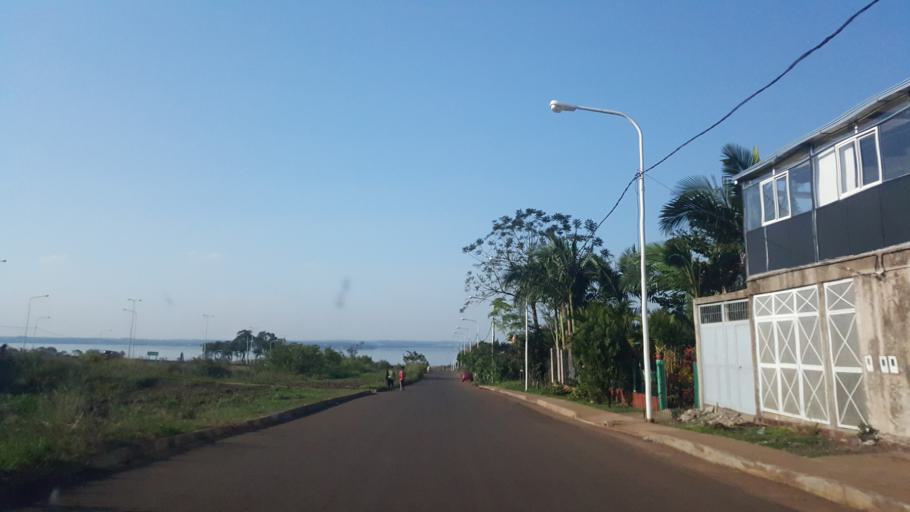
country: AR
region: Misiones
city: Garupa
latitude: -27.4492
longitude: -55.8530
